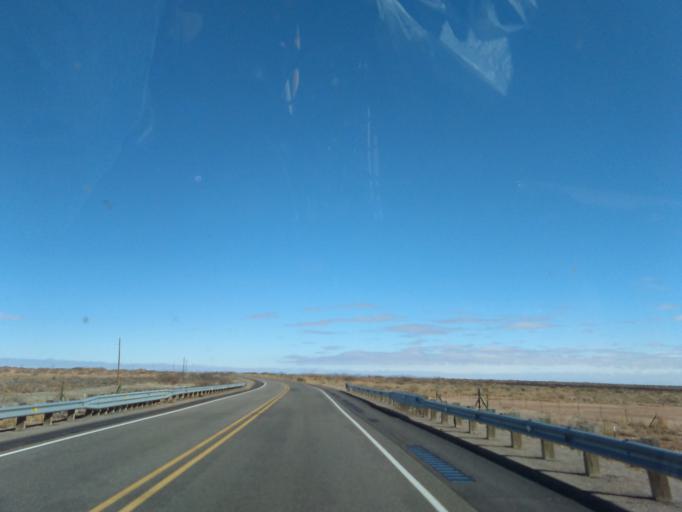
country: US
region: New Mexico
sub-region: Luna County
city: Deming
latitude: 32.2993
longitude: -107.7114
